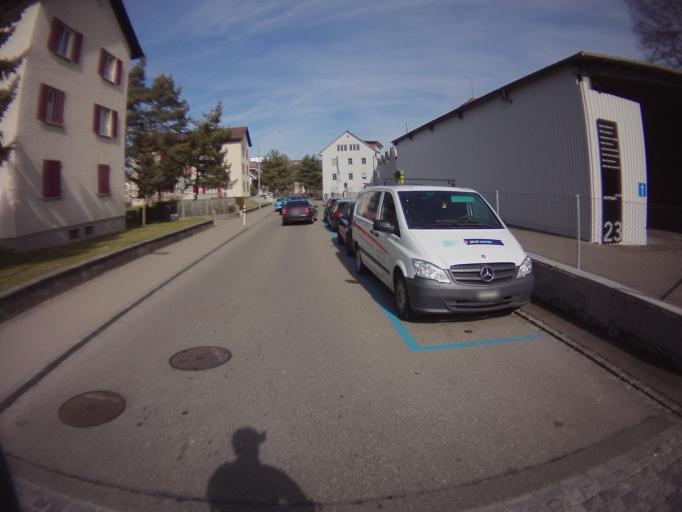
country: CH
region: Zurich
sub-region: Bezirk Dietikon
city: Dietikon
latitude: 47.4031
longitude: 8.3970
